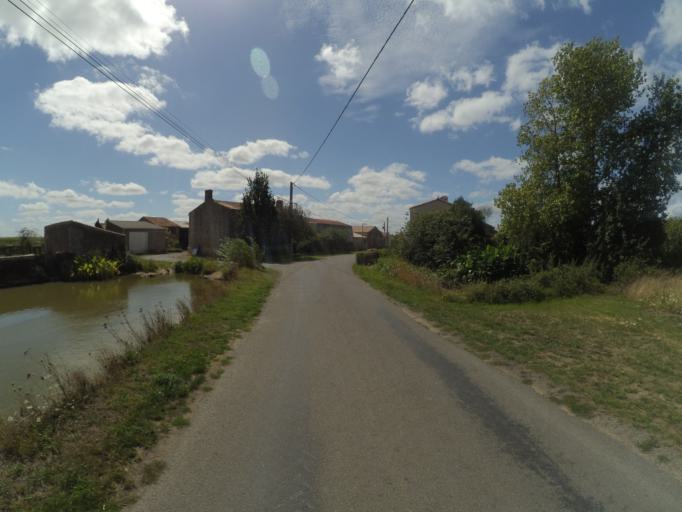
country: FR
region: Pays de la Loire
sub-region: Departement de la Loire-Atlantique
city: Saint-Hilaire-de-Clisson
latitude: 47.0734
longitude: -1.3136
